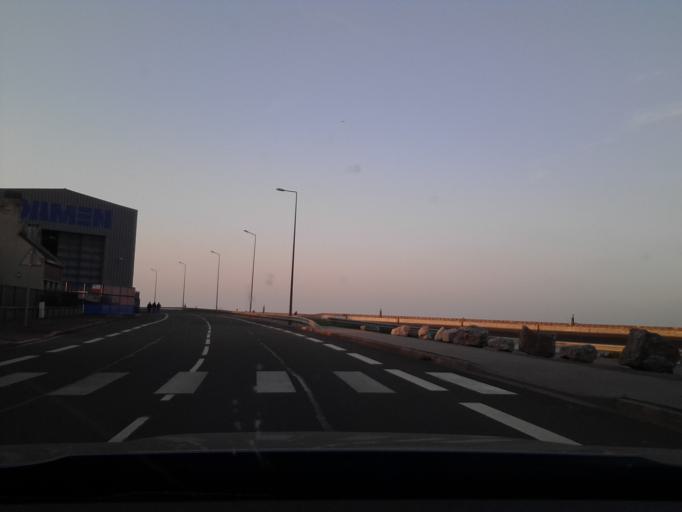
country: FR
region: Nord-Pas-de-Calais
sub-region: Departement du Nord
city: Dunkerque
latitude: 51.0488
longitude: 2.3647
